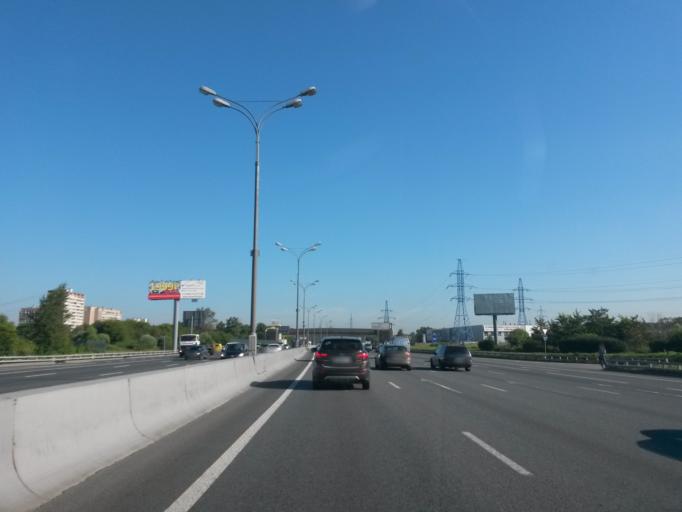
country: RU
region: Moscow
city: Gol'yanovo
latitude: 55.8156
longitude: 37.8387
